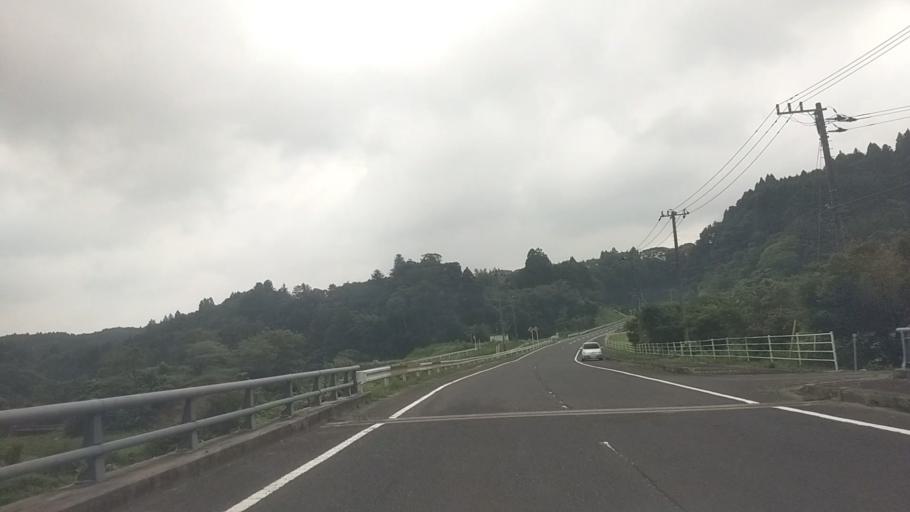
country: JP
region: Chiba
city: Kawaguchi
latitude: 35.2271
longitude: 140.1520
